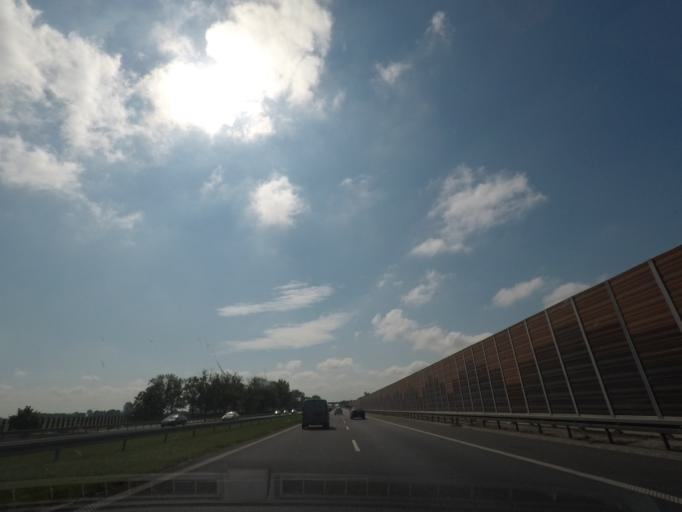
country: PL
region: Kujawsko-Pomorskie
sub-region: Powiat aleksandrowski
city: Raciazek
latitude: 52.8133
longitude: 18.8108
